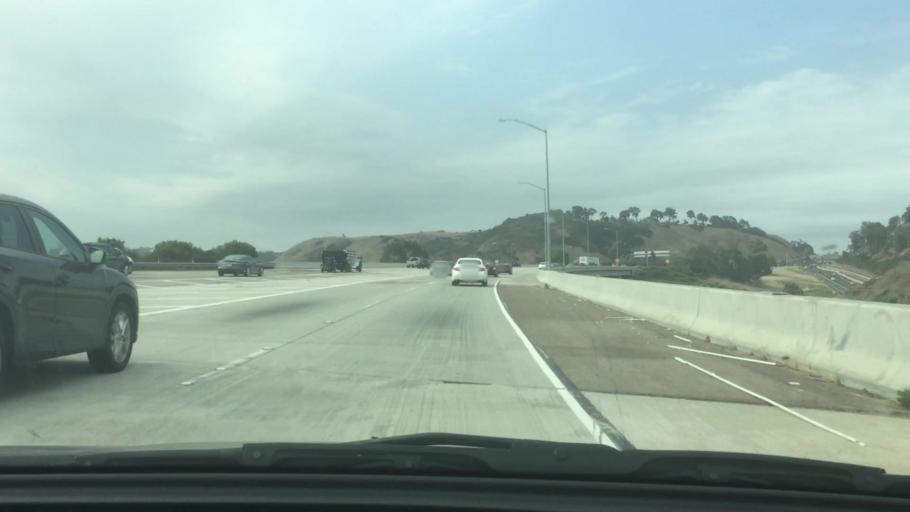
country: US
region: California
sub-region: San Diego County
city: Del Mar
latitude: 32.9039
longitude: -117.2249
